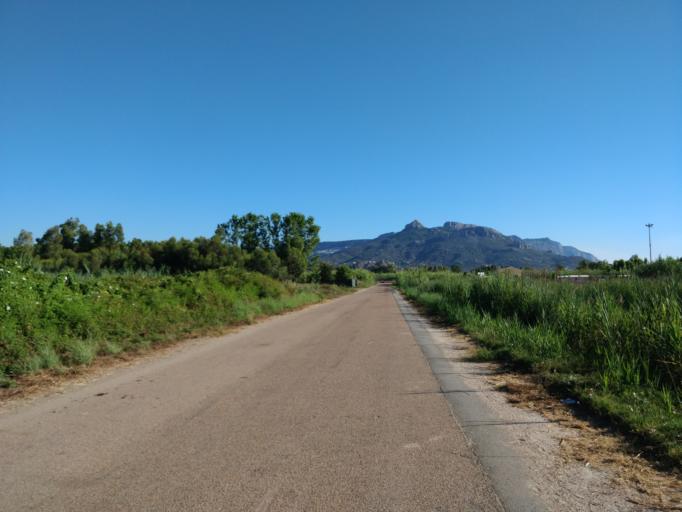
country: IT
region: Sardinia
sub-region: Provincia di Ogliastra
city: Lotzorai
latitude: 39.9585
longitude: 9.6774
